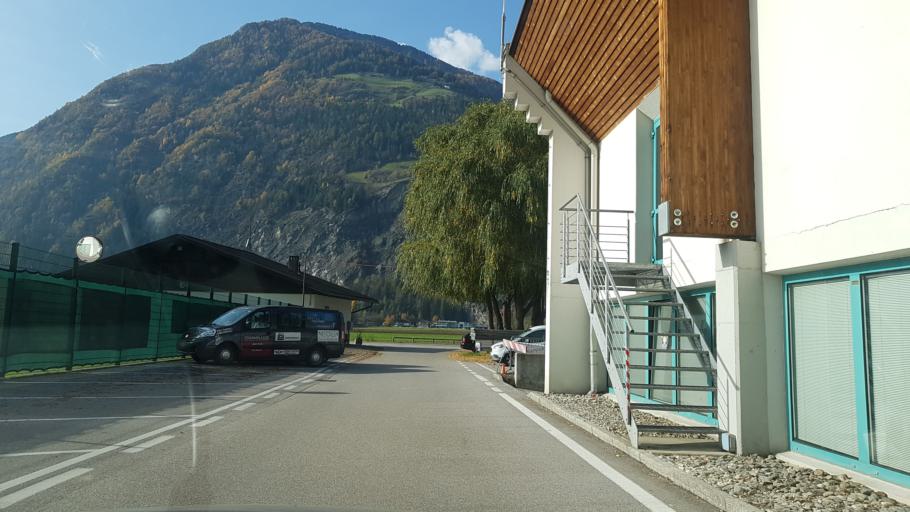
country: IT
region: Trentino-Alto Adige
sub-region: Bolzano
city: Campo Tures
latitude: 46.9110
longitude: 11.9618
